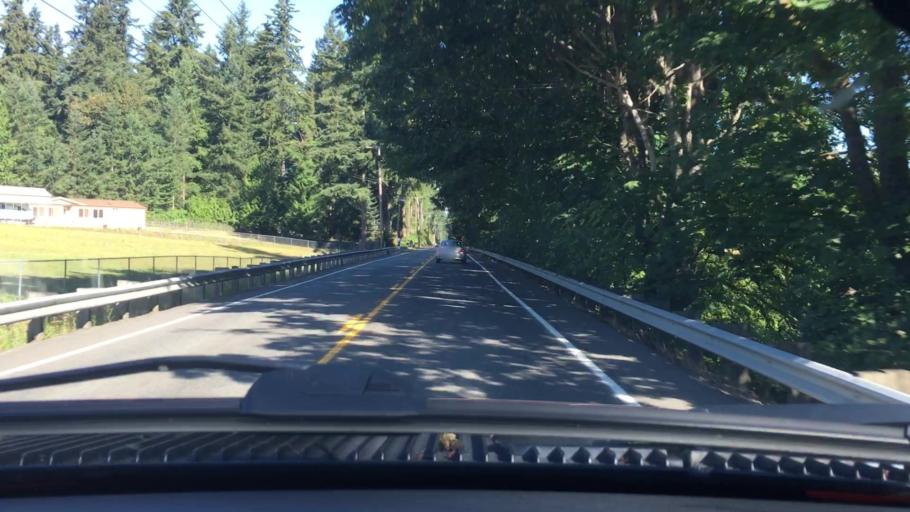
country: US
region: Washington
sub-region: King County
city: Lake Morton-Berrydale
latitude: 47.3265
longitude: -122.1139
